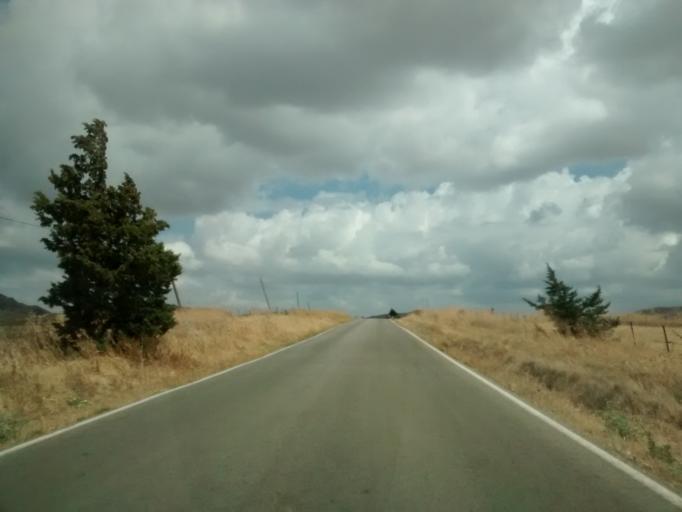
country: ES
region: Andalusia
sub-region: Provincia de Cadiz
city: Paterna de Rivera
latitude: 36.5032
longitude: -5.8834
